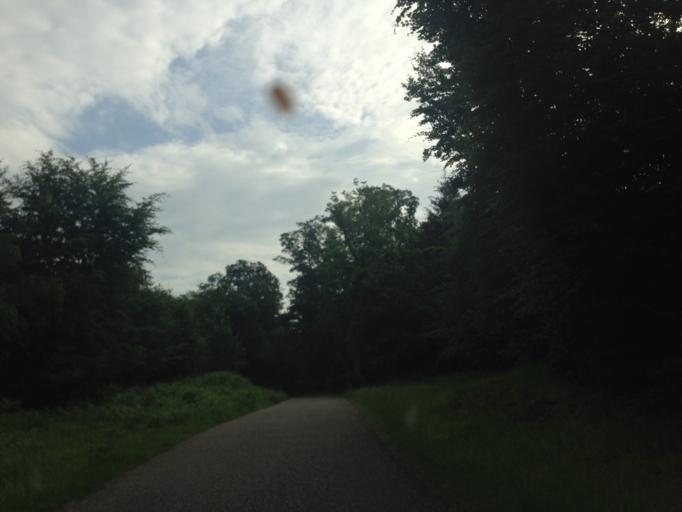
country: FR
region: Alsace
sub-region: Departement du Bas-Rhin
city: Neuwiller-les-Saverne
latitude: 48.8497
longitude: 7.3572
